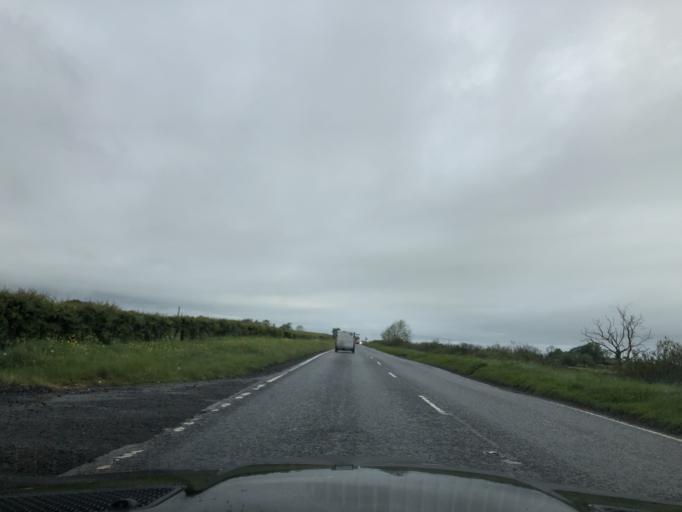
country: GB
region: Northern Ireland
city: Dunloy
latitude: 55.0197
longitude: -6.3760
